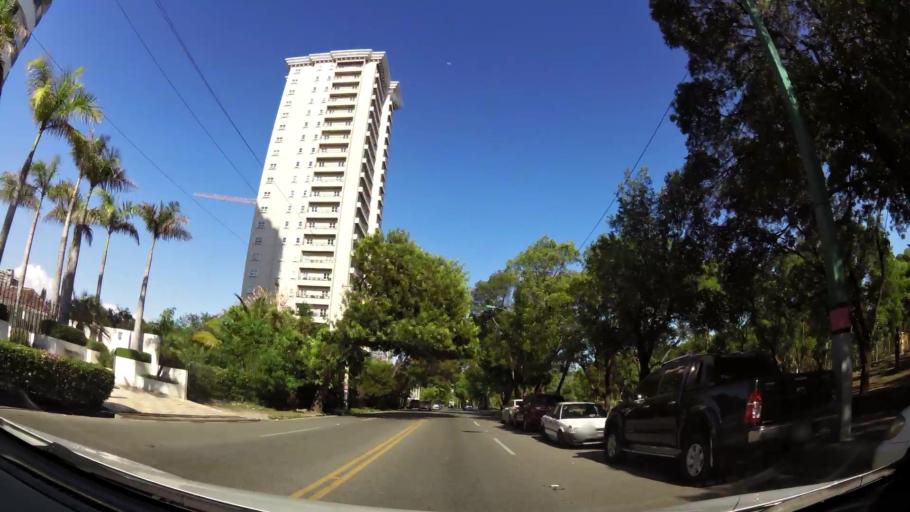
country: DO
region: Nacional
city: Bella Vista
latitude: 18.4371
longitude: -69.9753
